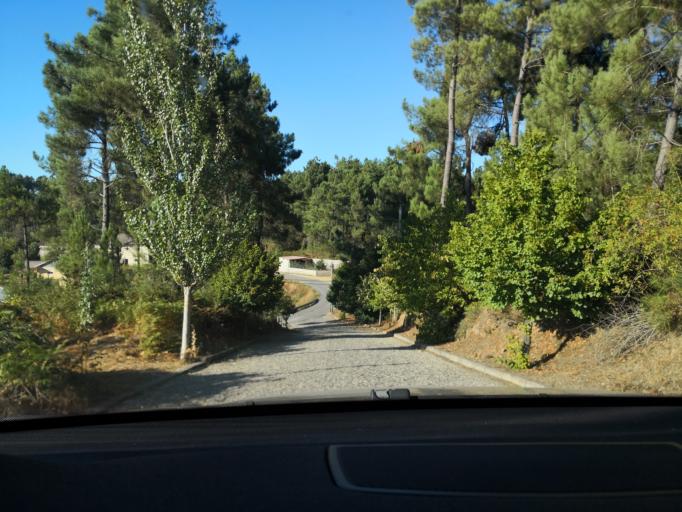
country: PT
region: Vila Real
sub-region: Sabrosa
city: Vilela
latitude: 41.2381
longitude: -7.6131
